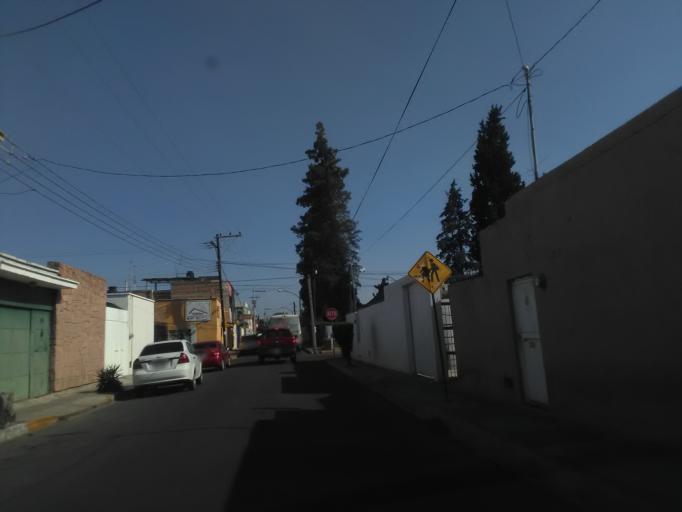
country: MX
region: Durango
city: Victoria de Durango
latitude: 24.0313
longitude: -104.6621
